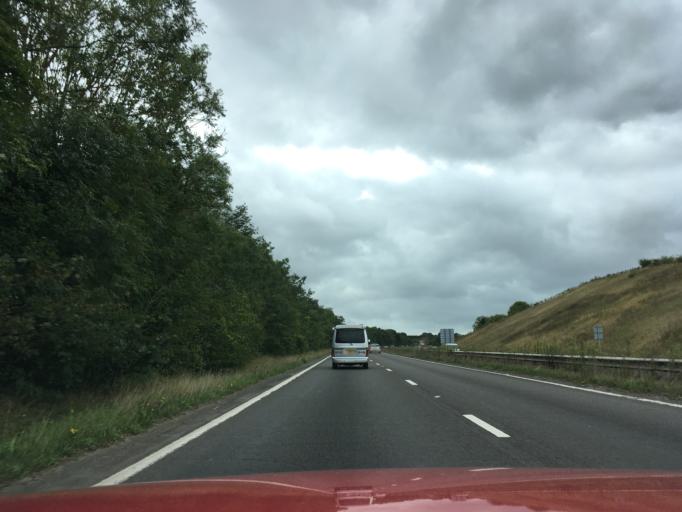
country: GB
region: England
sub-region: Devon
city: Kingskerswell
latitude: 50.4838
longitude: -3.5741
